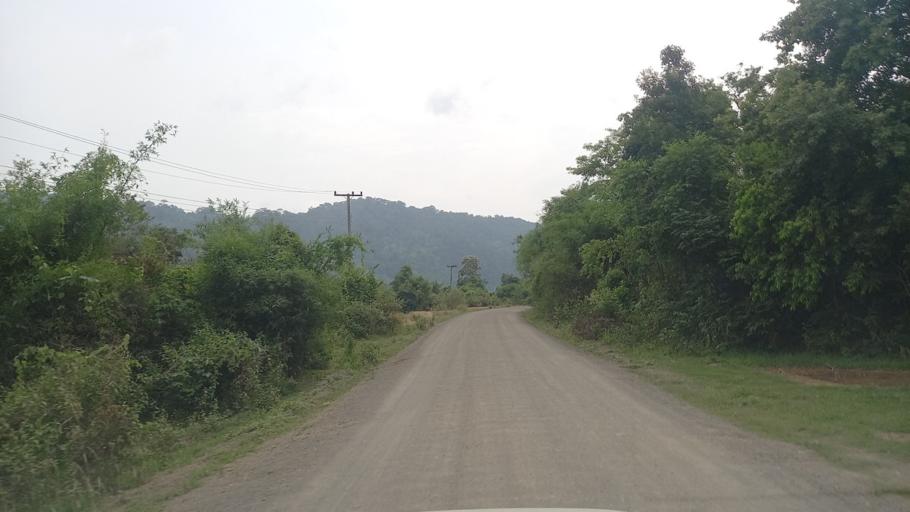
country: LA
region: Bolikhamxai
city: Ban Nahin
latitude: 18.1494
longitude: 104.7369
